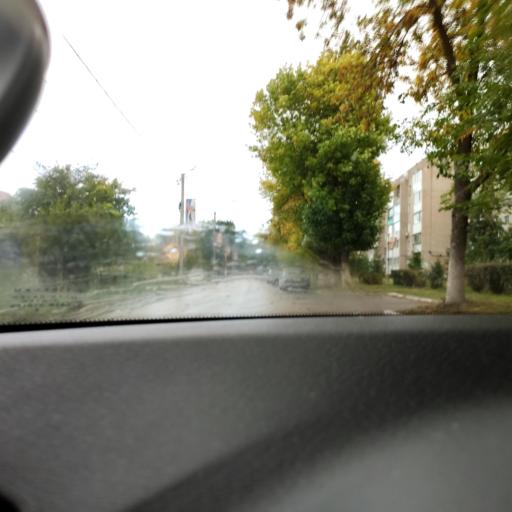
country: RU
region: Samara
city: Novosemeykino
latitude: 53.3706
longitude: 50.3597
